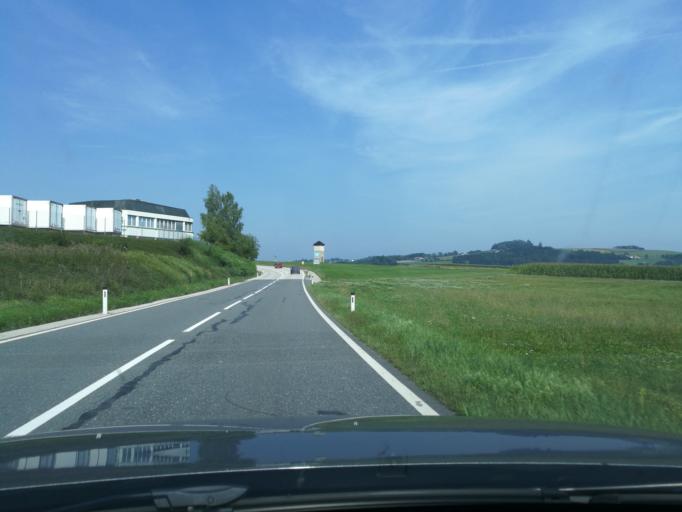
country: AT
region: Upper Austria
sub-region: Politischer Bezirk Grieskirchen
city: Grieskirchen
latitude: 48.3202
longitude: 13.7754
